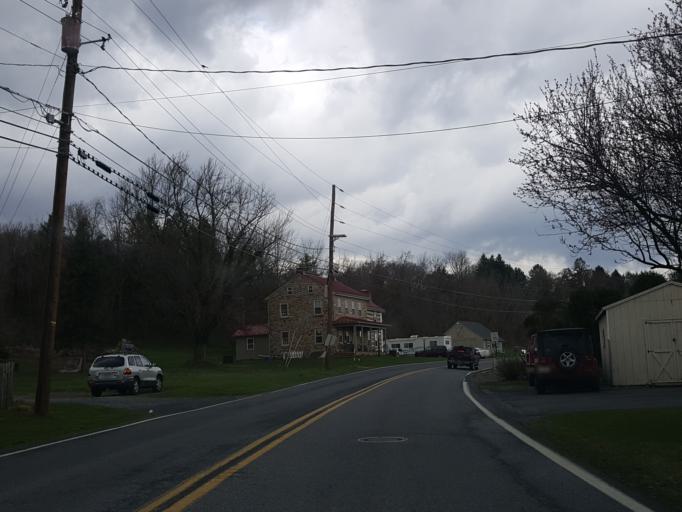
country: US
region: Pennsylvania
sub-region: Berks County
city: Fox Chase
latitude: 40.3927
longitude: -75.9943
